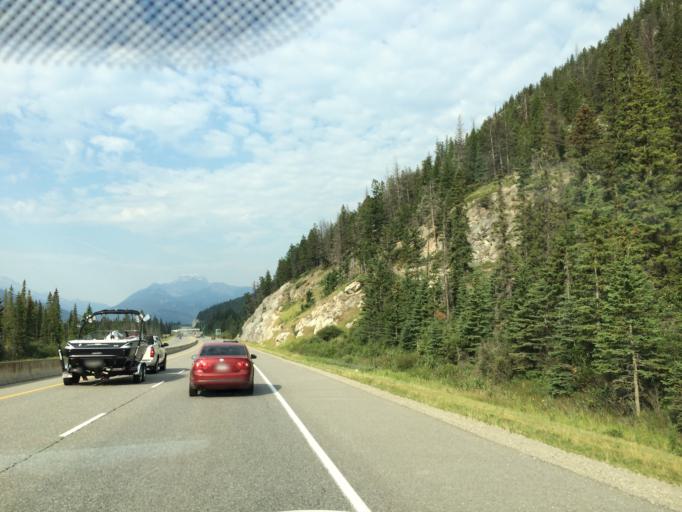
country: CA
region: Alberta
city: Banff
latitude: 51.1923
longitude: -115.5688
